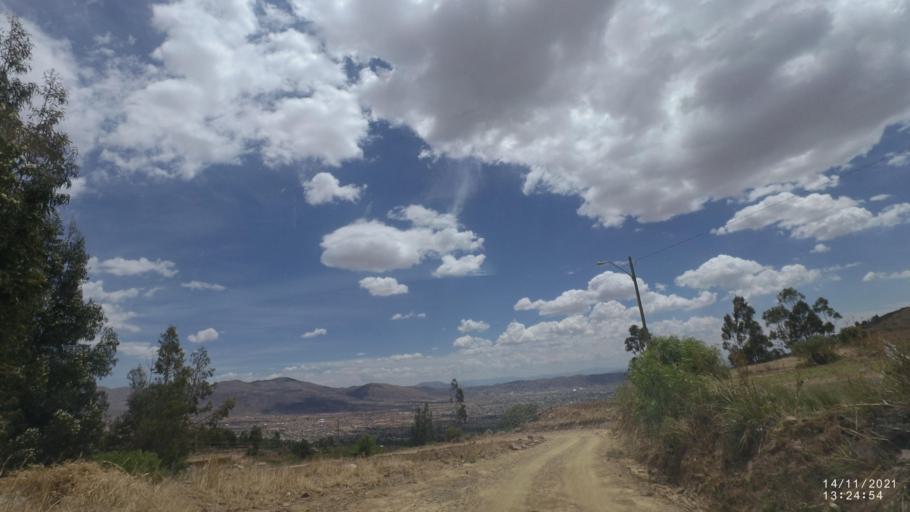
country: BO
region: Cochabamba
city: Colomi
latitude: -17.3795
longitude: -65.9807
